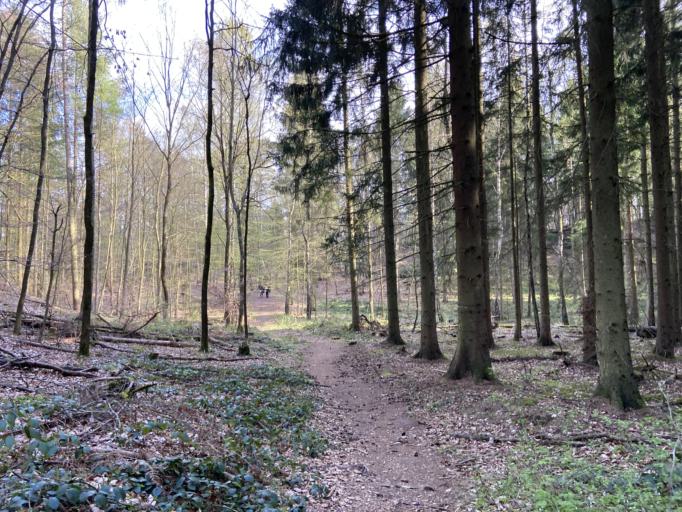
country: DE
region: Lower Saxony
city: Hahausen
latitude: 52.0051
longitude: 10.2138
